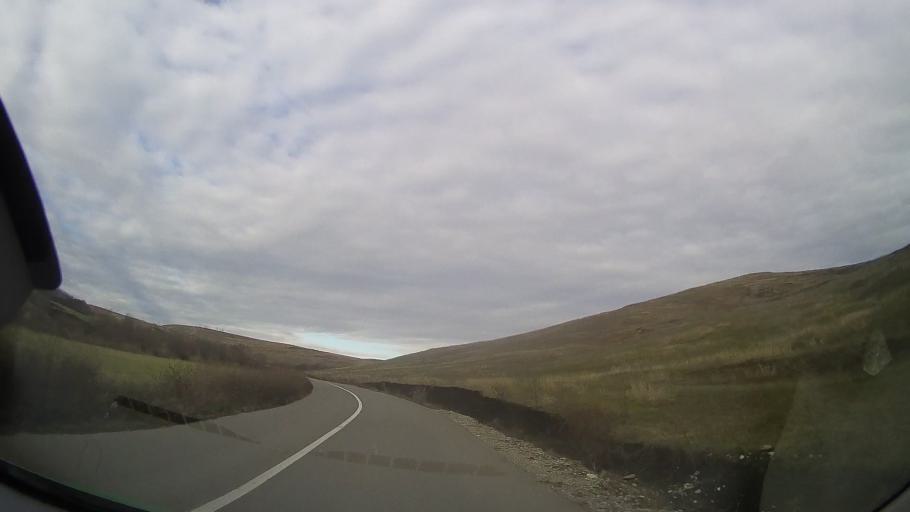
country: RO
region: Bistrita-Nasaud
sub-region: Comuna Silvasu de Campie
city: Silvasu de Campie
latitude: 46.8062
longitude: 24.2970
